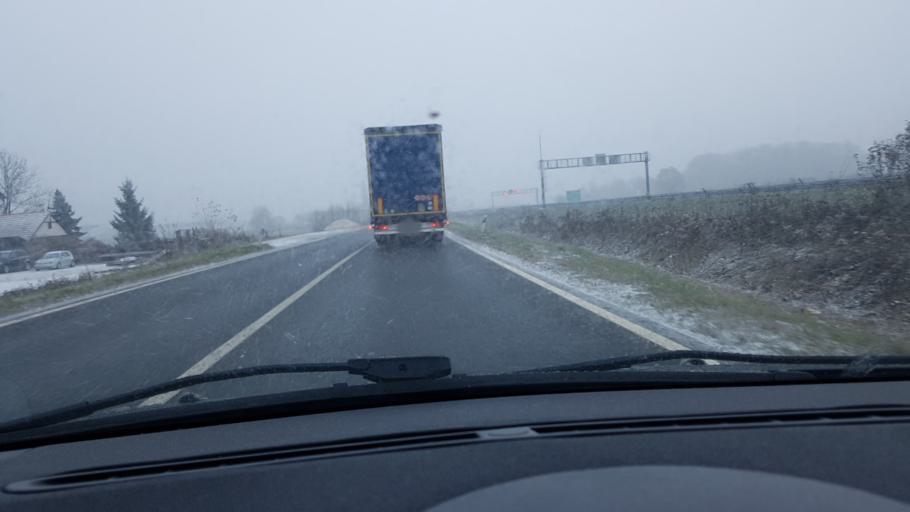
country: HR
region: Krapinsko-Zagorska
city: Oroslavje
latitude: 46.0028
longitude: 15.8655
